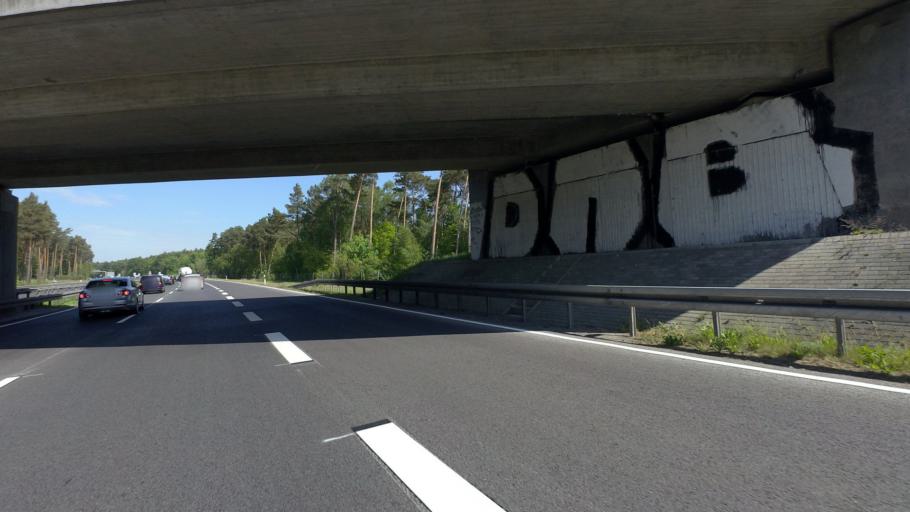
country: DE
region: Brandenburg
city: Oranienburg
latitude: 52.7961
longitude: 13.2346
